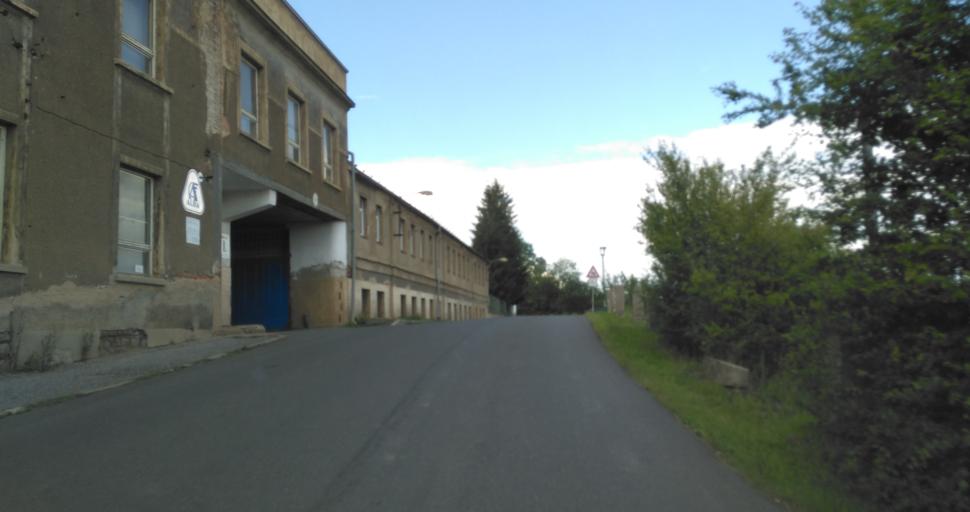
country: CZ
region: Central Bohemia
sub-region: Okres Beroun
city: Horovice
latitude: 49.8410
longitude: 13.8943
